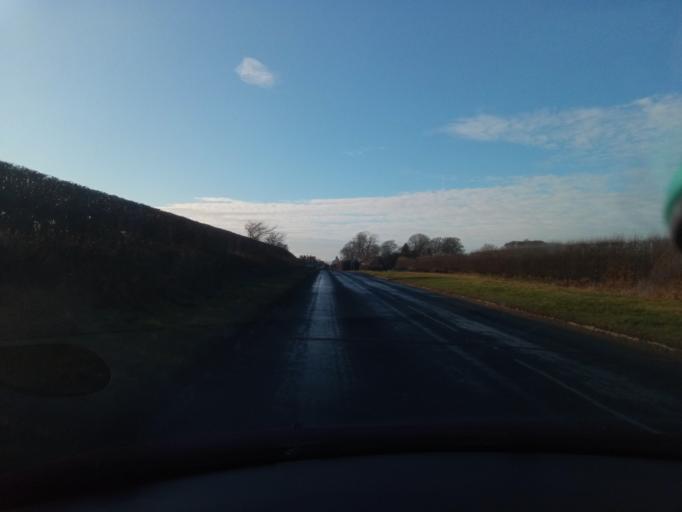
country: GB
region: England
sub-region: North Yorkshire
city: Thirsk
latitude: 54.2128
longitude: -1.4335
